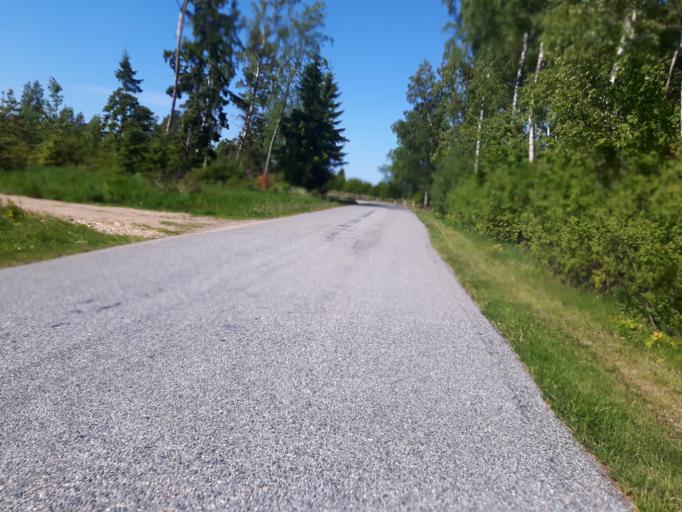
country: EE
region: Laeaene-Virumaa
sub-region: Haljala vald
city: Haljala
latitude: 59.5646
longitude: 26.3091
